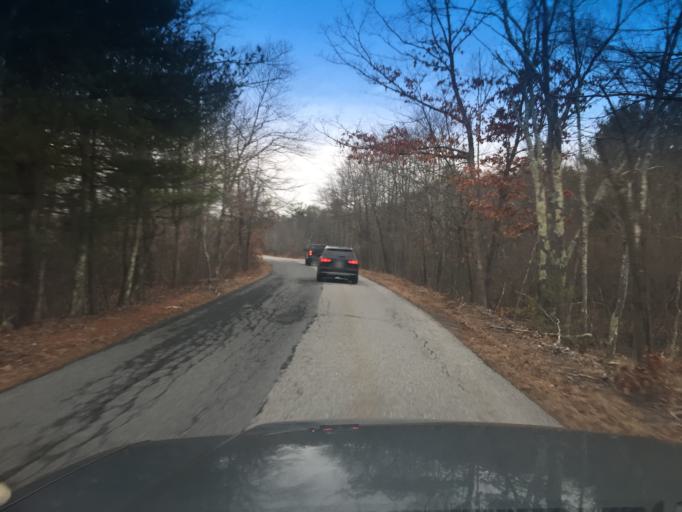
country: US
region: Massachusetts
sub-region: Norfolk County
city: Millis
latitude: 42.1758
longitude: -71.3849
